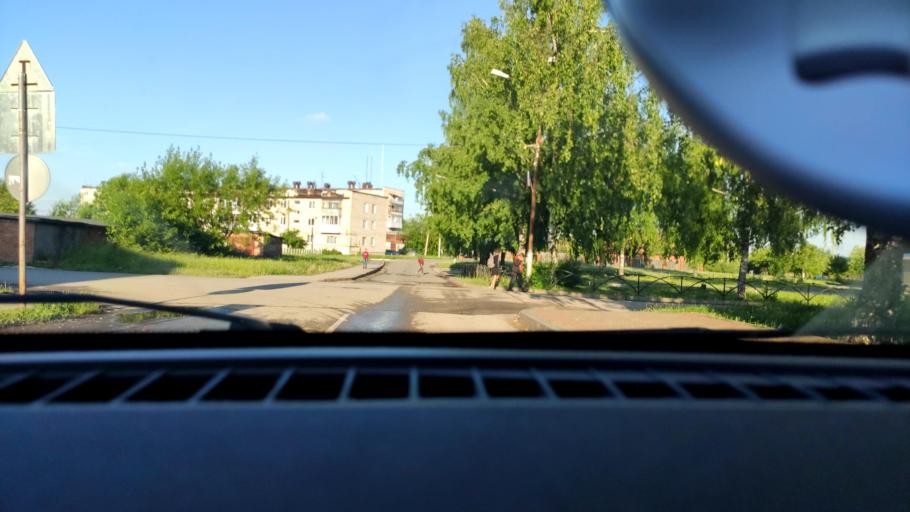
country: RU
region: Perm
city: Novyye Lyady
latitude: 58.0500
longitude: 56.5891
